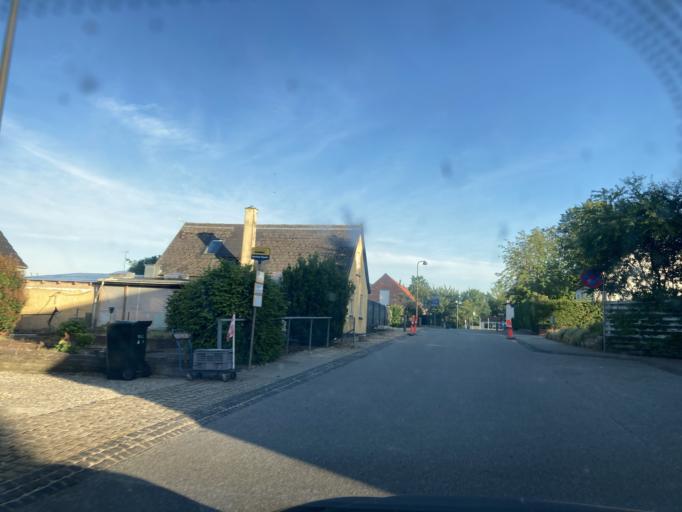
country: DK
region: Zealand
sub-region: Lejre Kommune
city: Lejre
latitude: 55.6417
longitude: 11.9610
